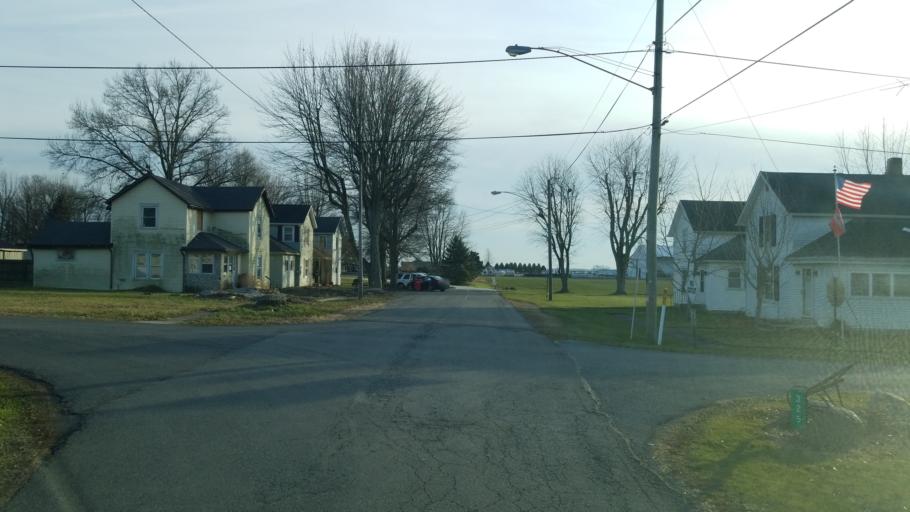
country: US
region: Ohio
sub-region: Marion County
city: Marion
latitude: 40.6834
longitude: -83.2136
